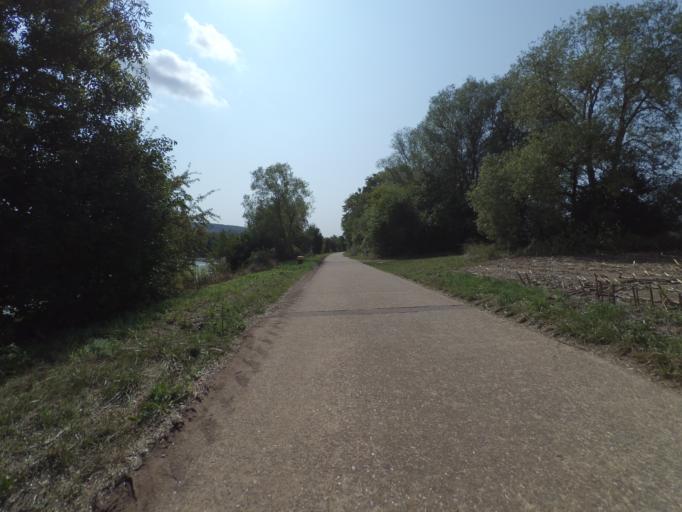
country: DE
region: Saarland
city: Merzig
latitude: 49.4487
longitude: 6.6309
